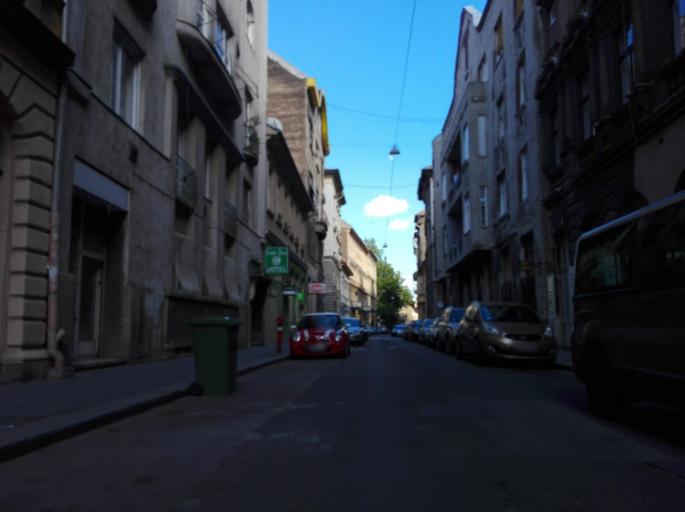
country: HU
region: Budapest
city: Budapest VI. keruelet
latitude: 47.5084
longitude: 19.0701
